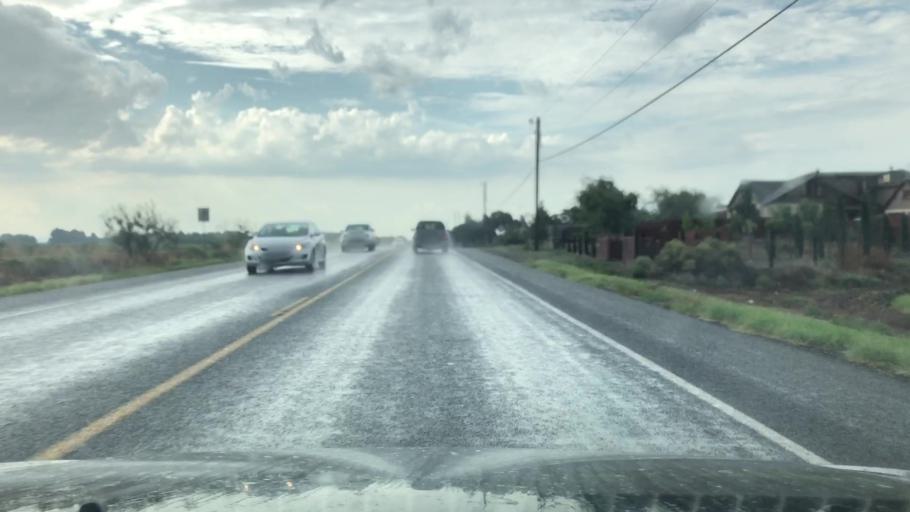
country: US
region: New Mexico
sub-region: Dona Ana County
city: Mesquite
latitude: 32.1868
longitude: -106.7106
